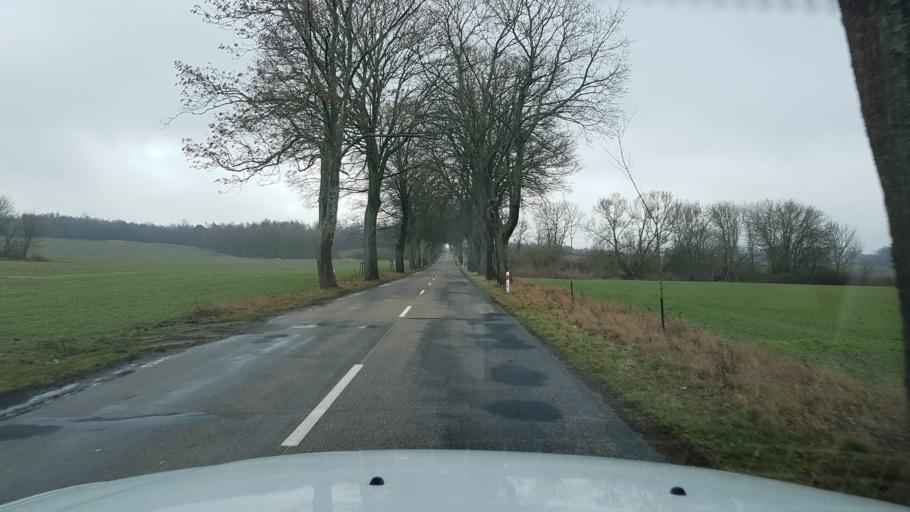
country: PL
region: West Pomeranian Voivodeship
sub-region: Powiat drawski
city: Czaplinek
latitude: 53.5771
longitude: 16.2361
